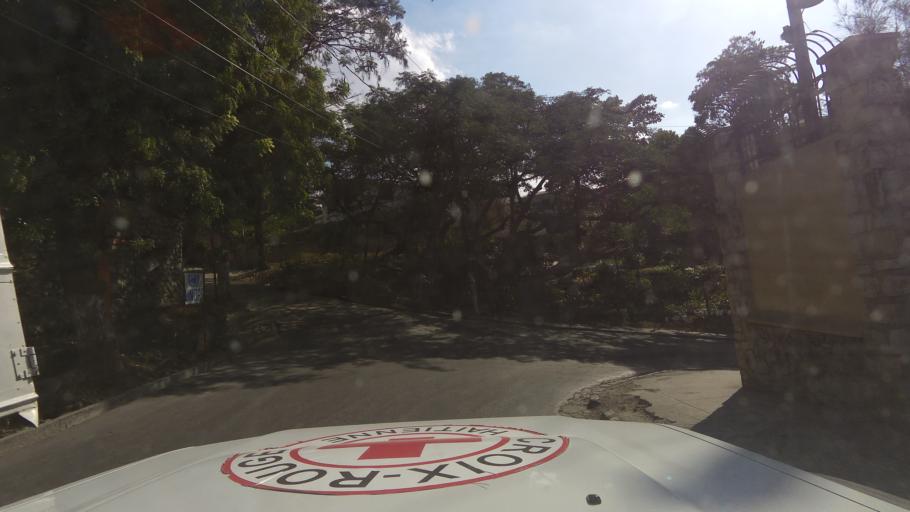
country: HT
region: Ouest
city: Petionville
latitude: 18.5146
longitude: -72.2743
